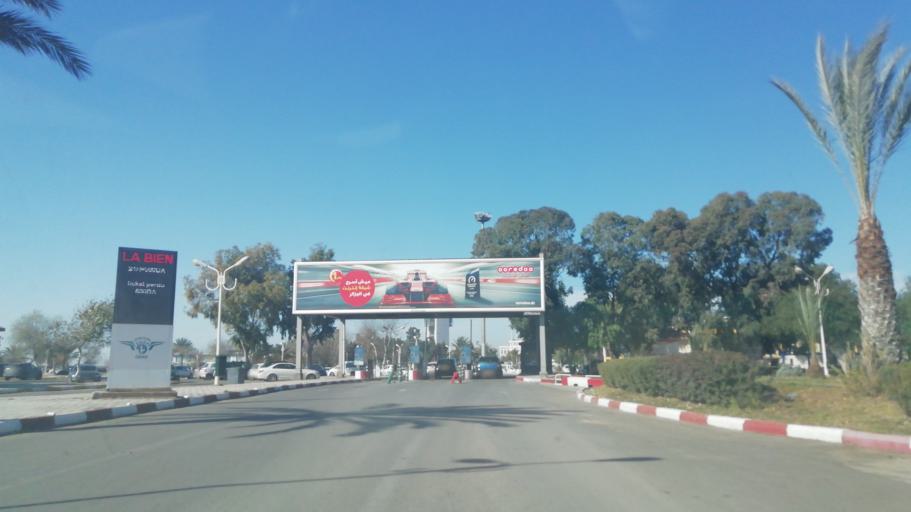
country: DZ
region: Oran
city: Es Senia
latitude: 35.6193
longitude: -0.6041
